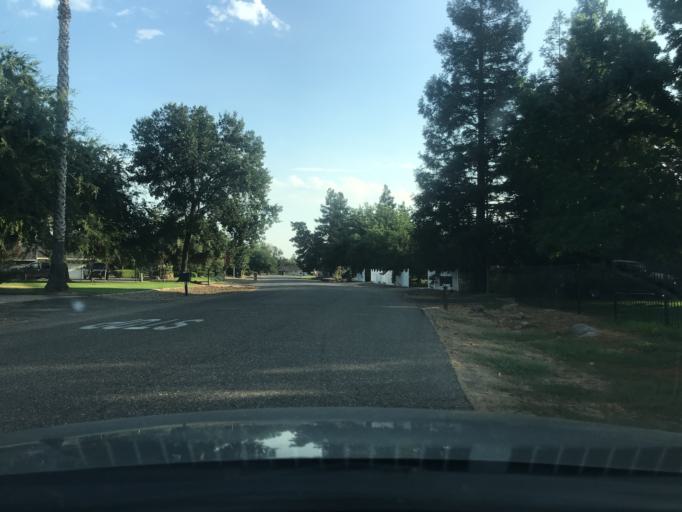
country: US
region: California
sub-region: Merced County
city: Atwater
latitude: 37.3503
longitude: -120.5750
